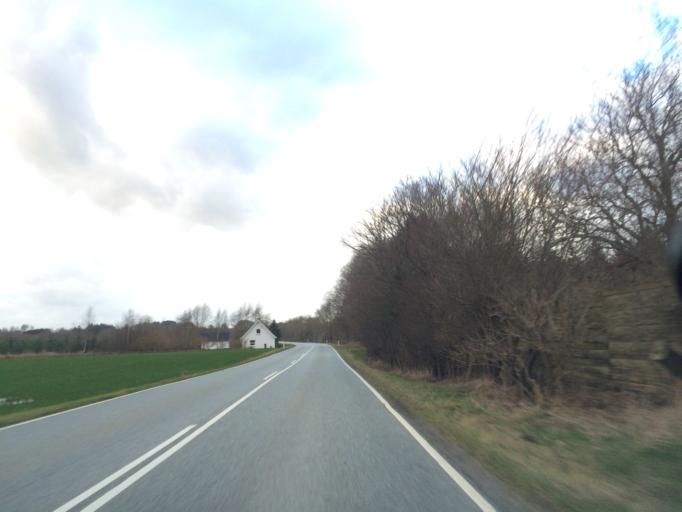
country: DK
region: Central Jutland
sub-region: Silkeborg Kommune
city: Virklund
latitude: 56.1034
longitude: 9.5924
